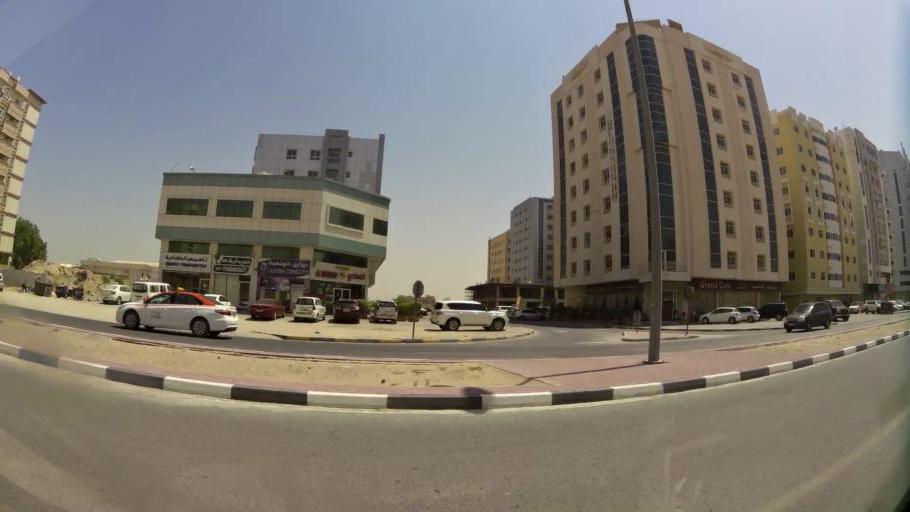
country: AE
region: Ajman
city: Ajman
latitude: 25.4083
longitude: 55.5102
